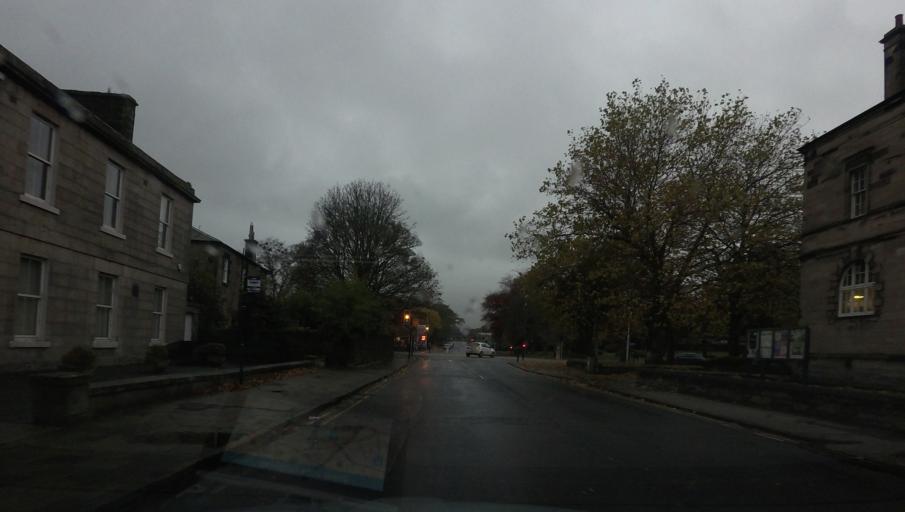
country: GB
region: Scotland
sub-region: Fife
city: Kirkcaldy
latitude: 56.1118
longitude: -3.1635
